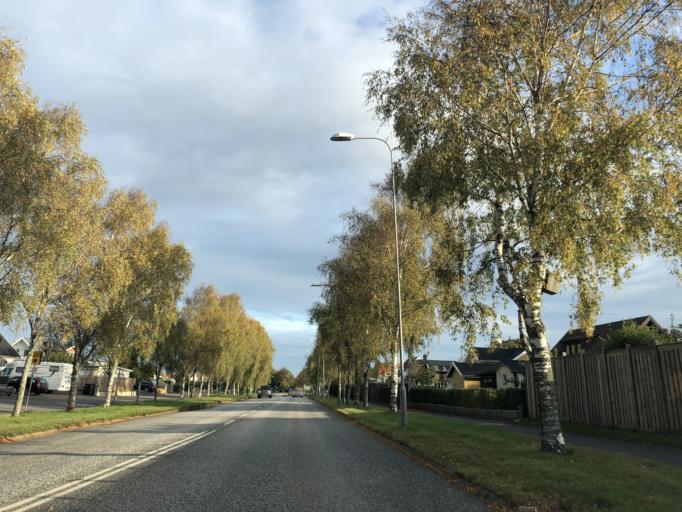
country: SE
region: Vaestra Goetaland
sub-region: Goteborg
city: Majorna
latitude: 57.6613
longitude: 11.8727
